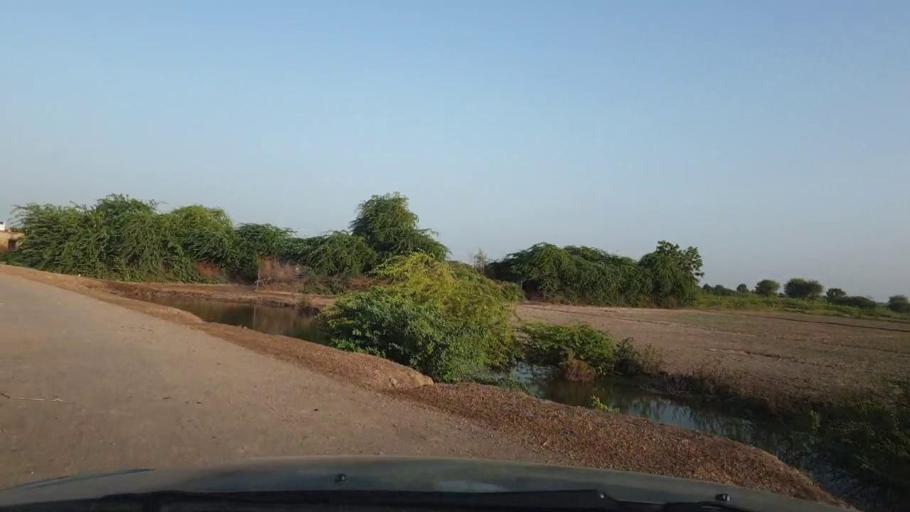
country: PK
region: Sindh
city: Tando Ghulam Ali
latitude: 25.1224
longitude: 68.9647
